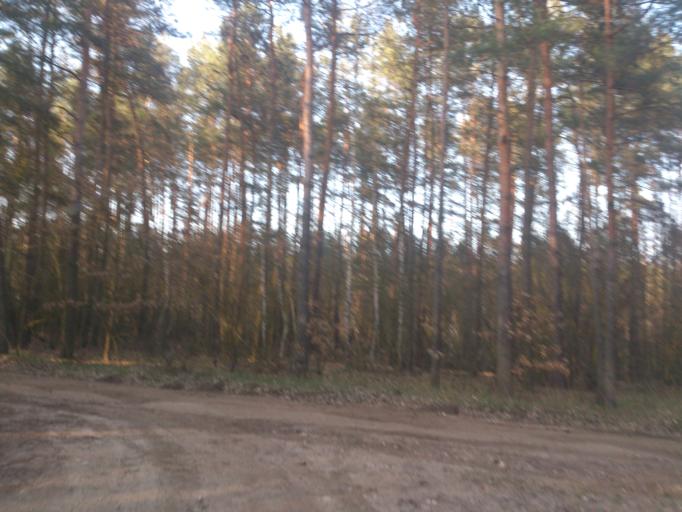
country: PL
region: Kujawsko-Pomorskie
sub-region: Powiat golubsko-dobrzynski
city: Radomin
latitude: 53.1369
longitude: 19.1580
